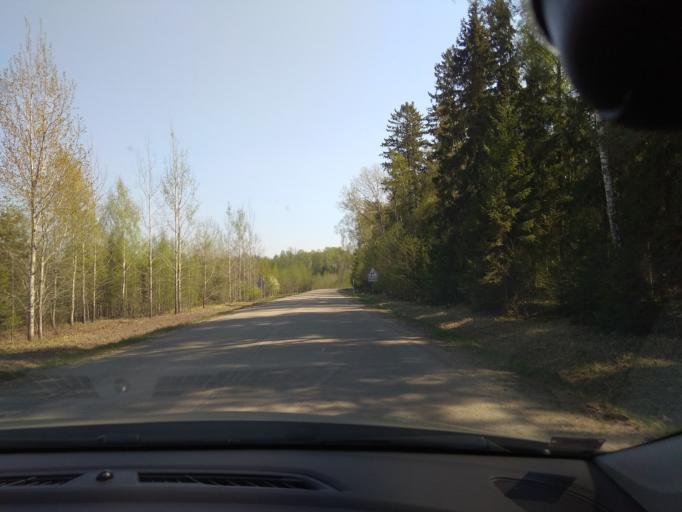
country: LT
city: Linkuva
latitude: 55.9811
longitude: 24.1823
